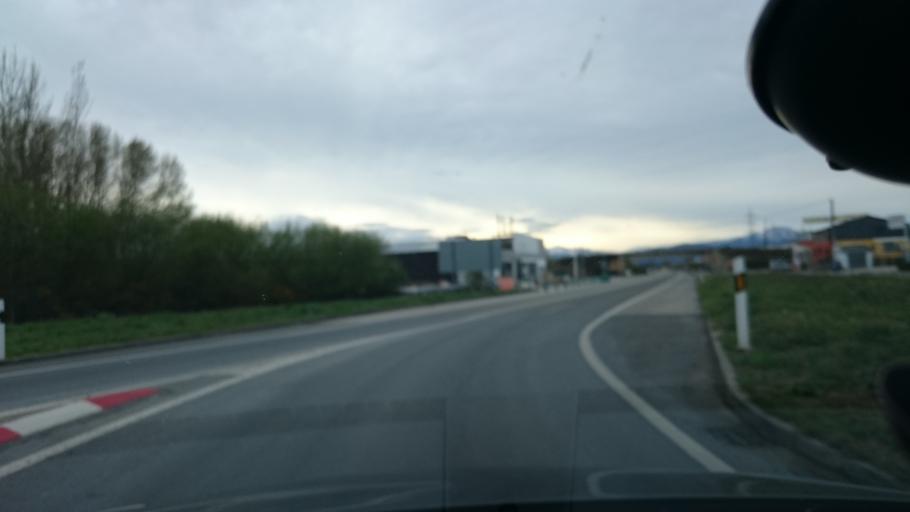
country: ES
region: Castille and Leon
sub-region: Provincia de Leon
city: Camponaraya
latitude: 42.5661
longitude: -6.6589
